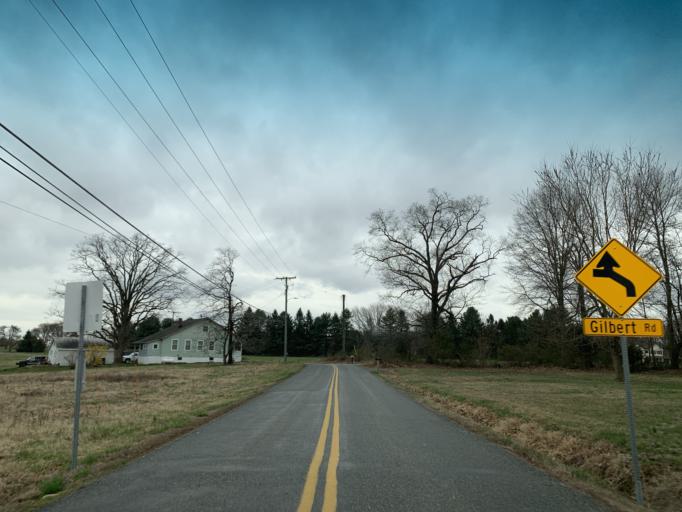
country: US
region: Maryland
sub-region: Harford County
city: Aberdeen
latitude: 39.5547
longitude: -76.1961
